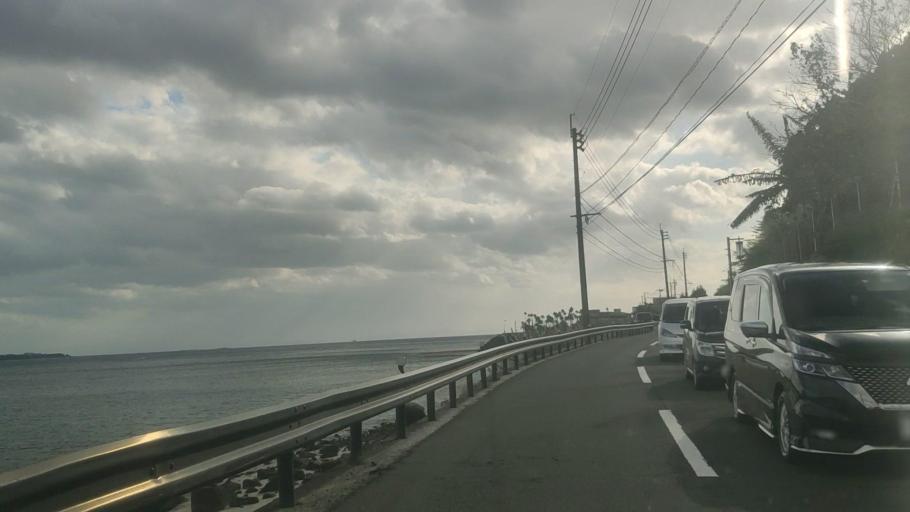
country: JP
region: Kagoshima
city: Kagoshima-shi
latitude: 31.6123
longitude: 130.5754
